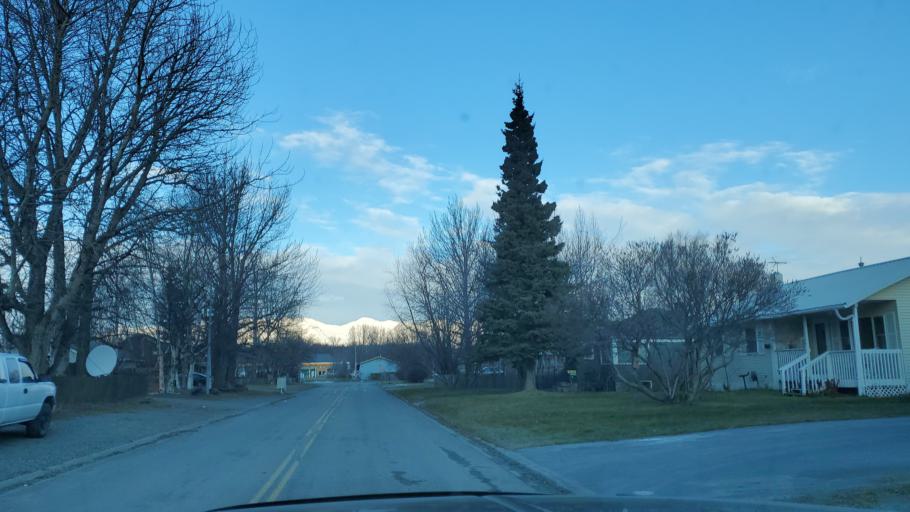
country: US
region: Alaska
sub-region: Matanuska-Susitna Borough
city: Palmer
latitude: 61.6045
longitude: -149.1165
